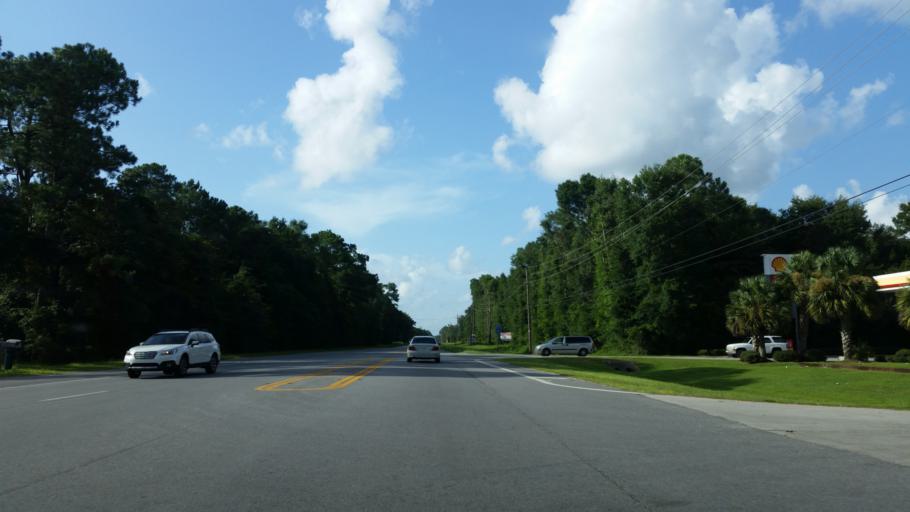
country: US
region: Florida
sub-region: Santa Rosa County
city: Bagdad
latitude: 30.5724
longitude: -87.0314
